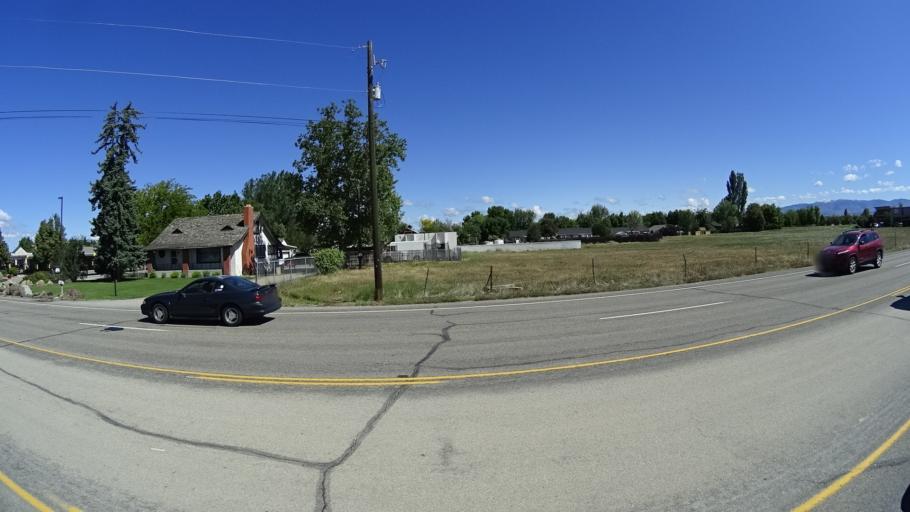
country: US
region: Idaho
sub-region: Ada County
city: Meridian
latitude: 43.6194
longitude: -116.3664
